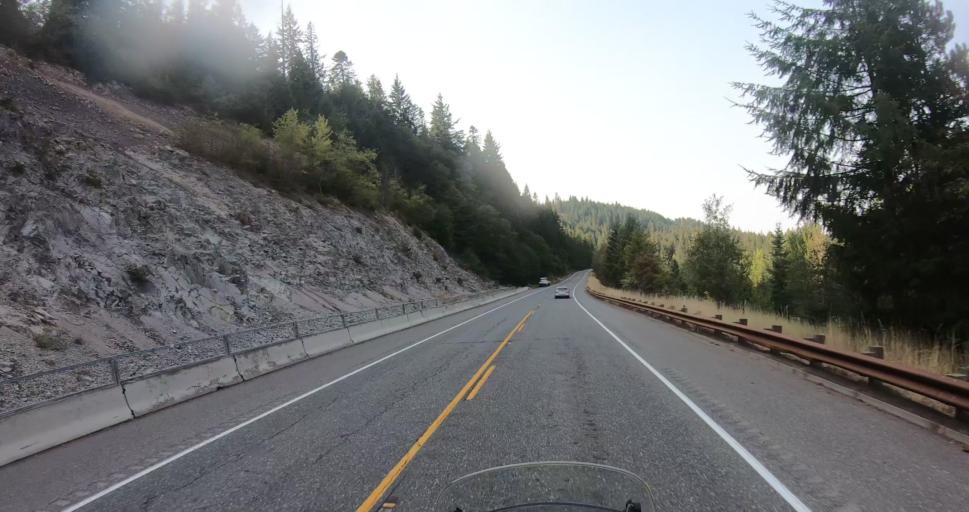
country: US
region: Oregon
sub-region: Hood River County
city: Odell
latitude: 45.4437
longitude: -121.5784
